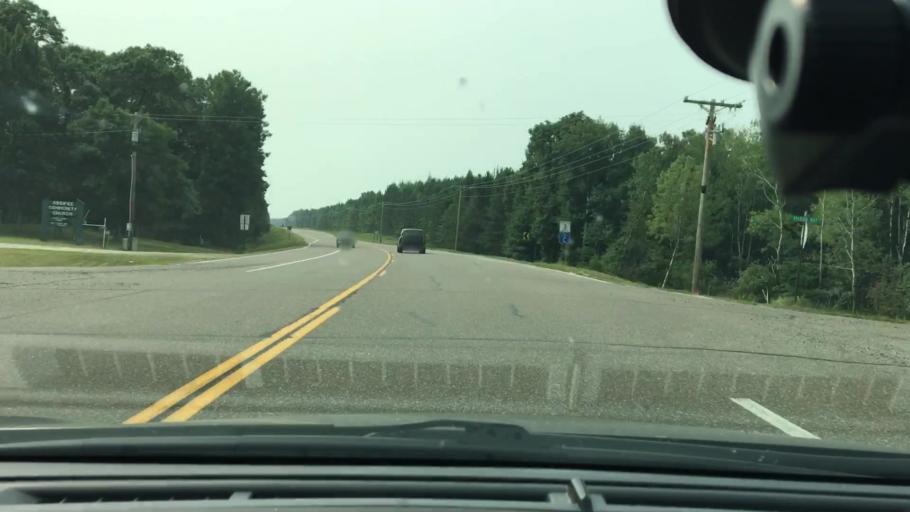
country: US
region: Minnesota
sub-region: Crow Wing County
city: Breezy Point
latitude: 46.5591
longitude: -94.1354
